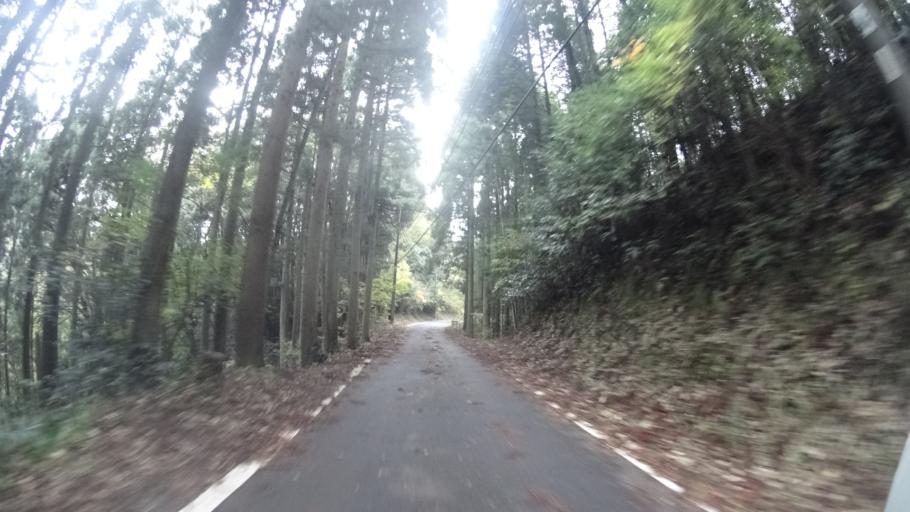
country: JP
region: Kyoto
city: Maizuru
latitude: 35.4916
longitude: 135.4647
